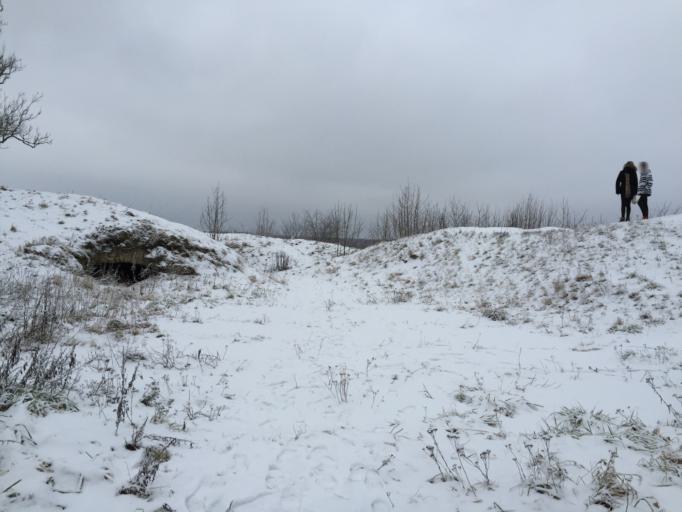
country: EE
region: Laeaene
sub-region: Lihula vald
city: Lihula
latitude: 58.6945
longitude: 23.8391
